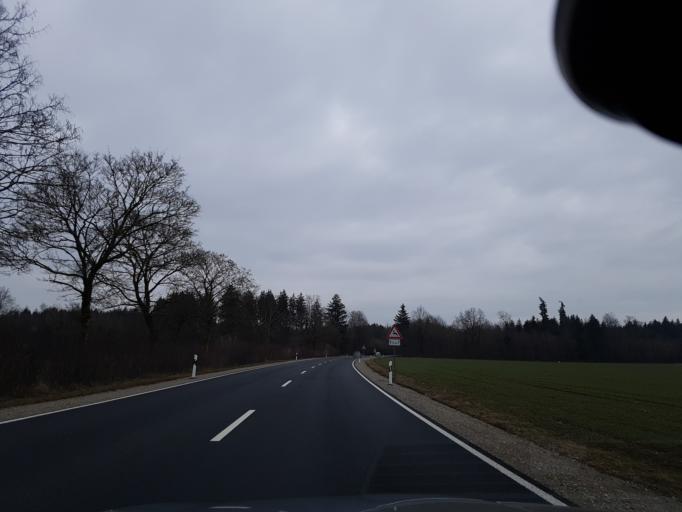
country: DE
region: Bavaria
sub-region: Upper Bavaria
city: Hohenkirchen-Siegertsbrunn
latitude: 47.9844
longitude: 11.7218
